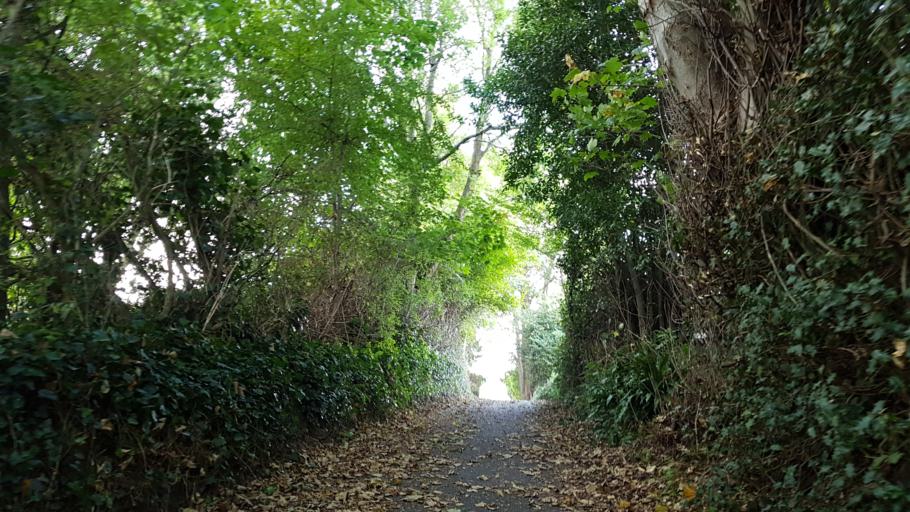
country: GB
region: England
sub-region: Isle of Wight
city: Ryde
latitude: 50.7316
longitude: -1.1836
